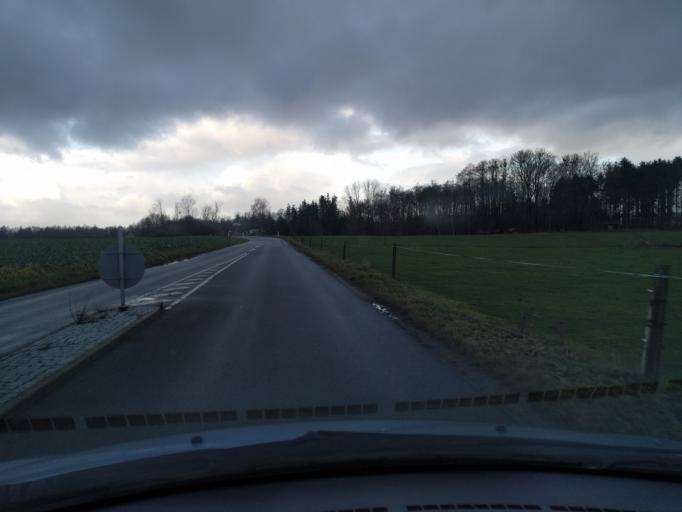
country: DK
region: South Denmark
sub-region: Kerteminde Kommune
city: Langeskov
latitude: 55.3656
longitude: 10.5872
